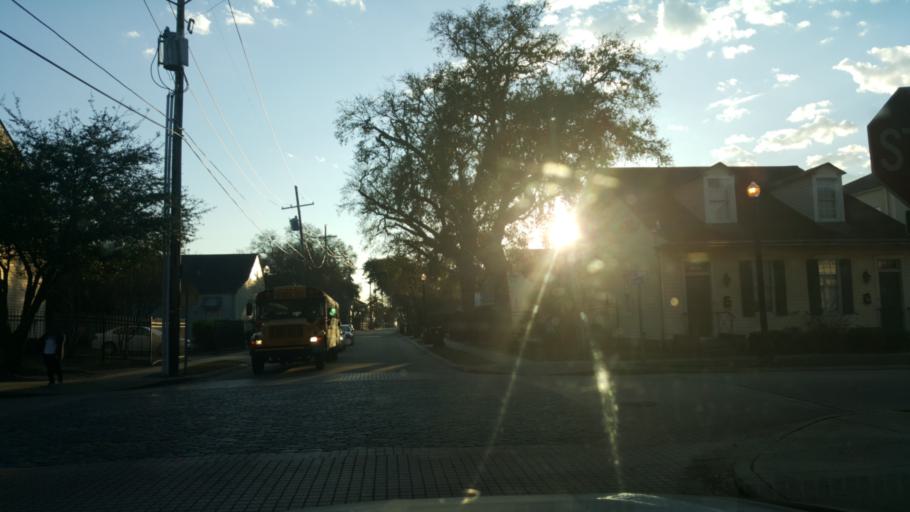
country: US
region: Louisiana
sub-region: Jefferson Parish
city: Gretna
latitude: 29.9295
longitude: -90.0714
